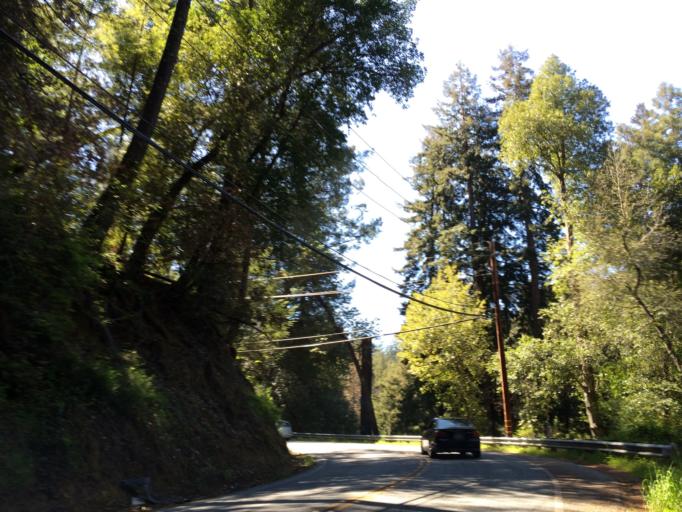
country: US
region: California
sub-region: Santa Clara County
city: Lexington Hills
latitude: 37.1785
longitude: -122.0096
